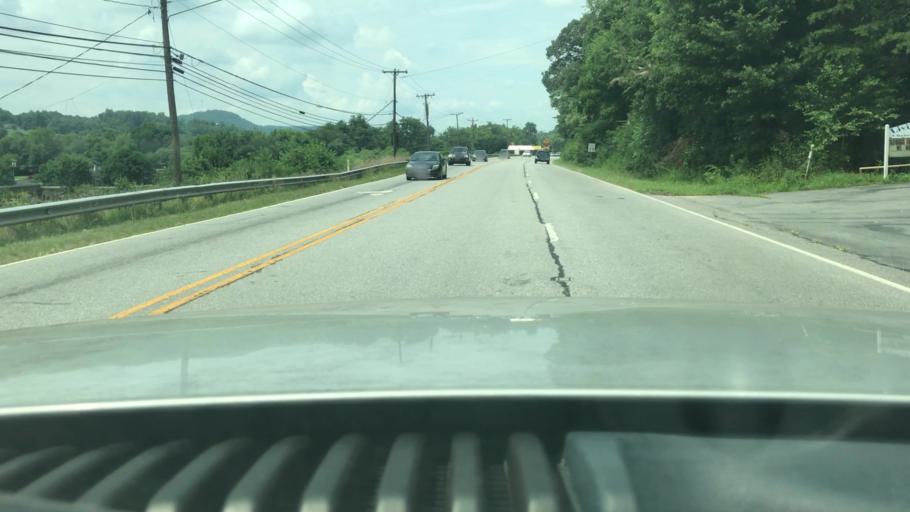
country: US
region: North Carolina
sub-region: Wilkes County
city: Wilkesboro
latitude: 36.1567
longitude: -81.1619
